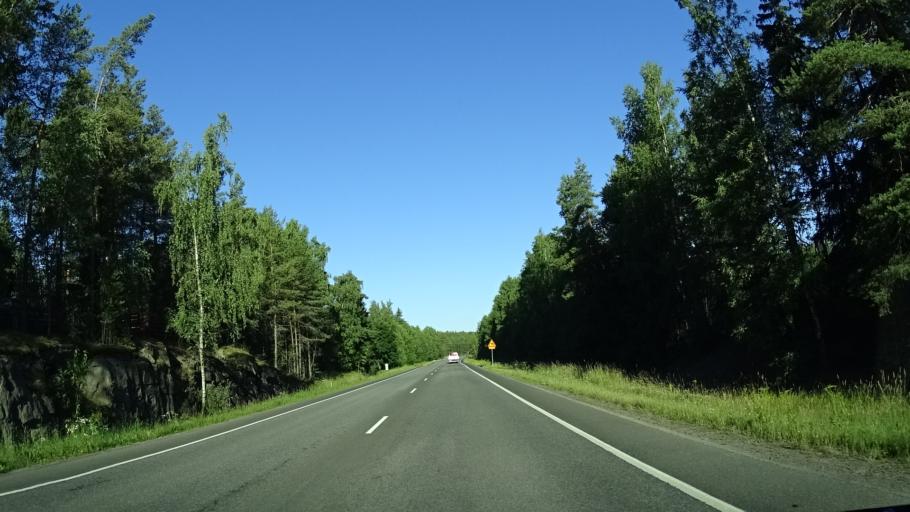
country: FI
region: Varsinais-Suomi
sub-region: Turku
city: Naantali
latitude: 60.4596
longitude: 21.9568
